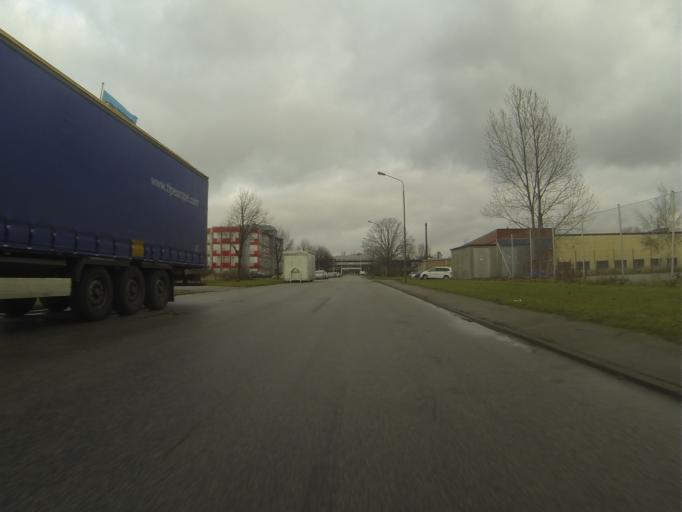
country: SE
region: Skane
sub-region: Burlovs Kommun
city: Arloev
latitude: 55.6471
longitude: 13.0872
